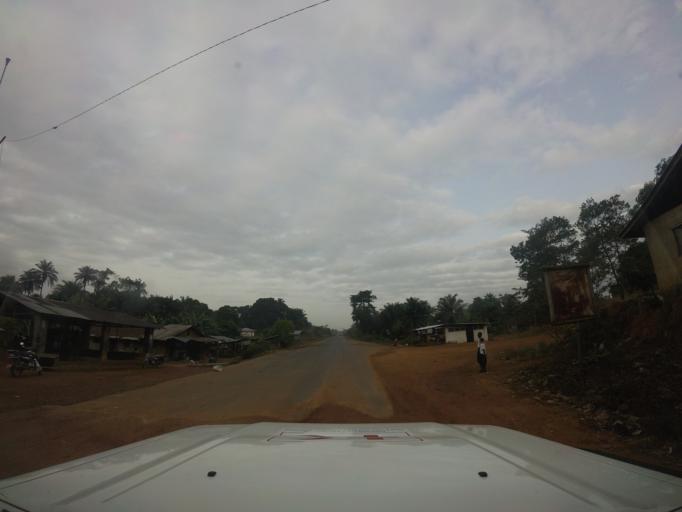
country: LR
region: Bomi
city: Tubmanburg
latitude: 6.7290
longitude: -11.0225
